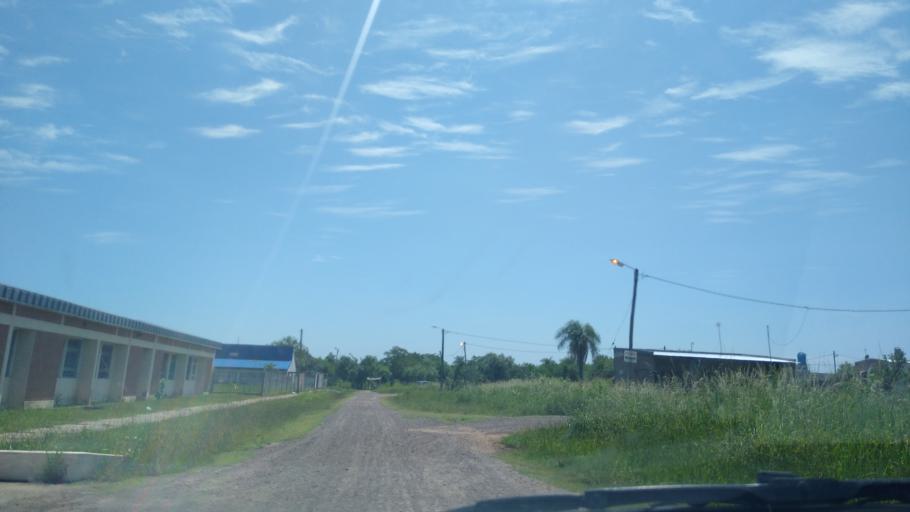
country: AR
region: Chaco
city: Fontana
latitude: -27.4028
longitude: -59.0453
